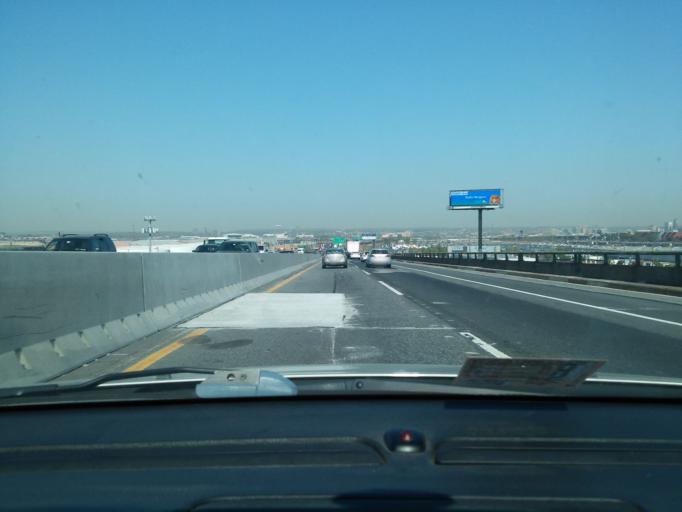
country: US
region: New Jersey
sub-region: Hudson County
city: Bayonne
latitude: 40.6993
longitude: -74.1313
